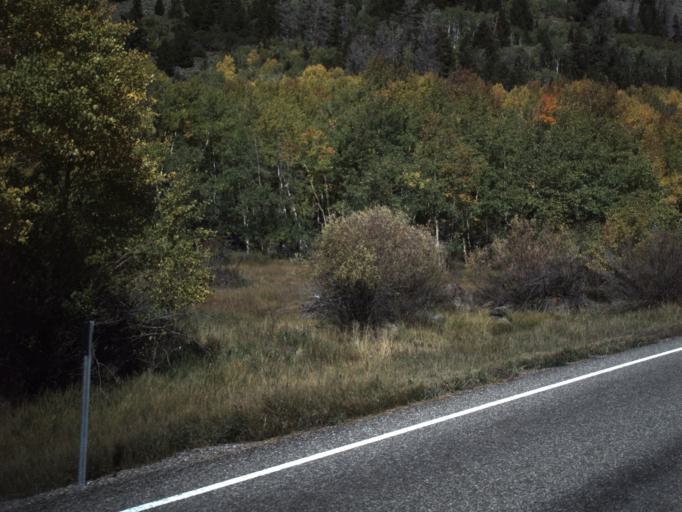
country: US
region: Utah
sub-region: Wayne County
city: Loa
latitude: 38.5359
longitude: -111.7379
